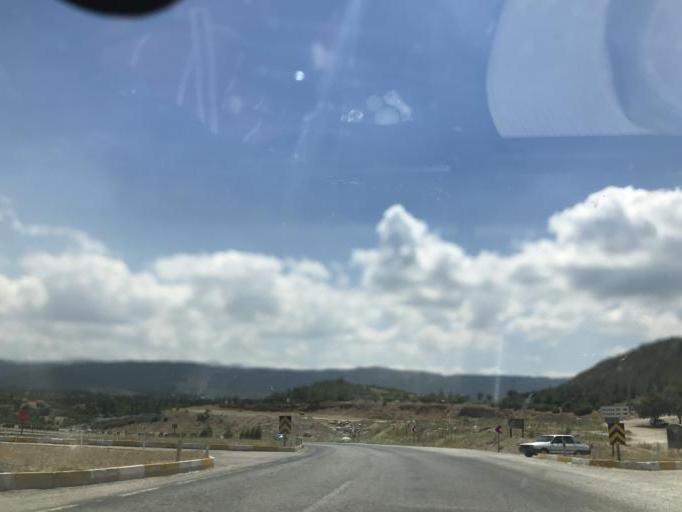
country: TR
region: Denizli
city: Honaz
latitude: 37.7014
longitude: 29.2004
